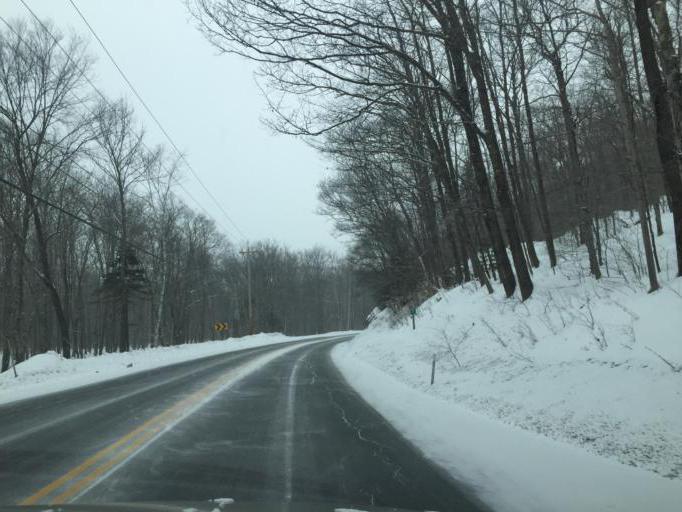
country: US
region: New Hampshire
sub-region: Carroll County
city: North Conway
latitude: 44.1711
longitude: -71.2229
